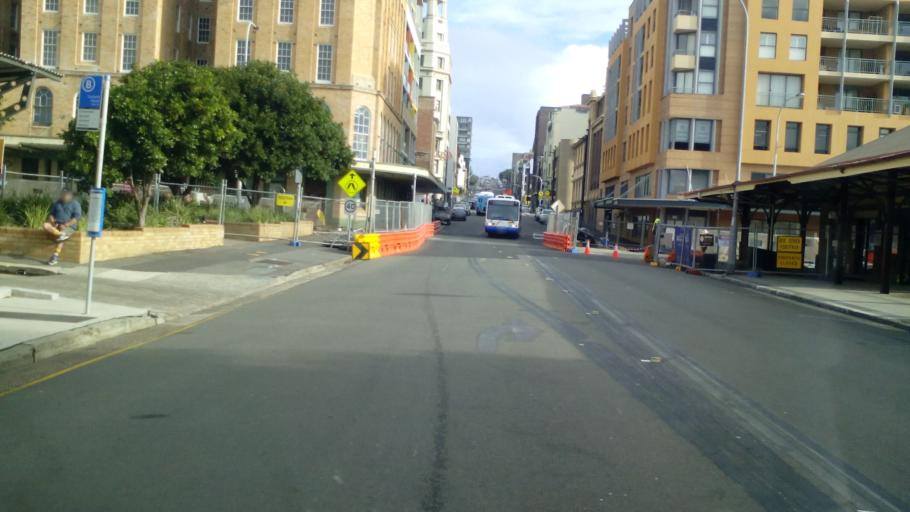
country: AU
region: New South Wales
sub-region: Newcastle
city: Newcastle
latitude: -32.9266
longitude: 151.7848
